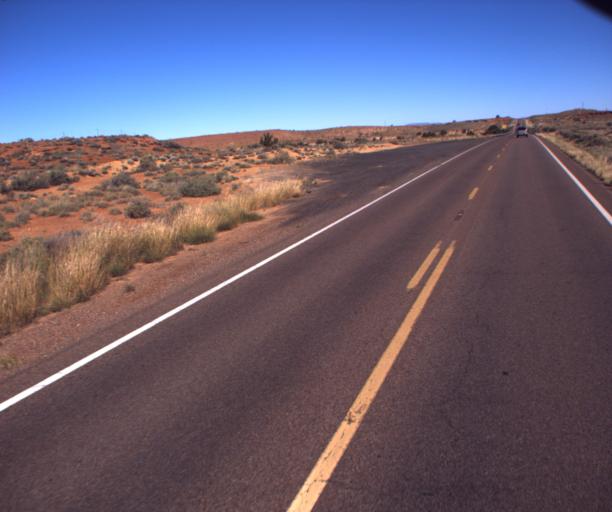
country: US
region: Arizona
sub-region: Navajo County
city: Holbrook
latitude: 34.8352
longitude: -110.1446
